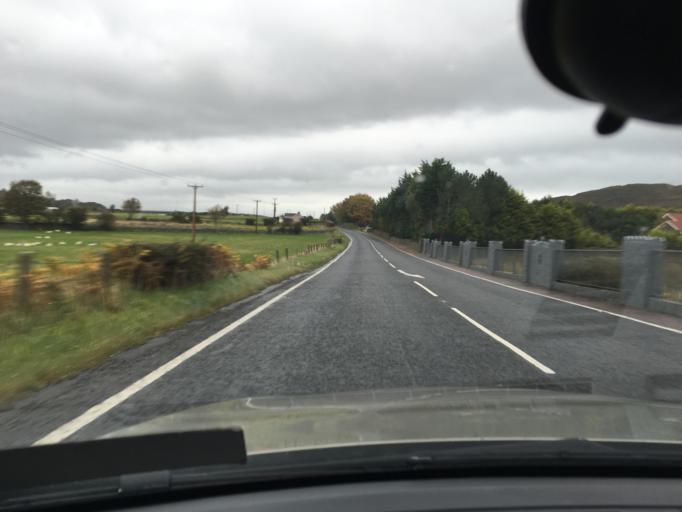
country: GB
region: Northern Ireland
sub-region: Newry and Mourne District
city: Newry
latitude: 54.1330
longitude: -6.3447
